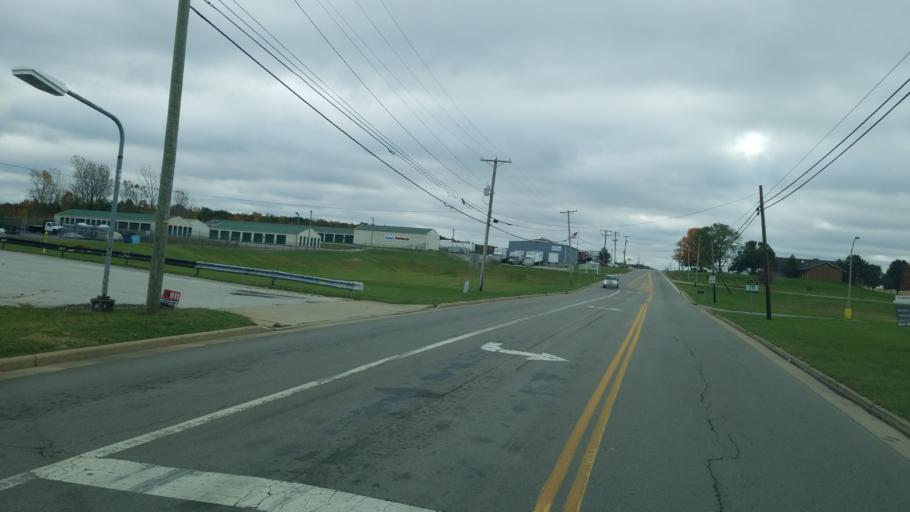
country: US
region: Ohio
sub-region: Huron County
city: Willard
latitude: 41.0426
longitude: -82.7324
